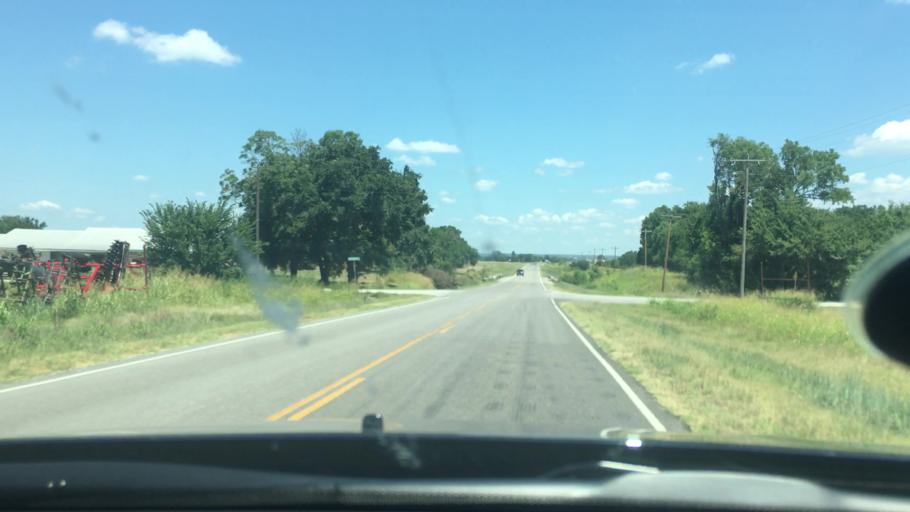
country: US
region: Oklahoma
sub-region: Carter County
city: Dickson
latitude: 34.2155
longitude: -96.9771
